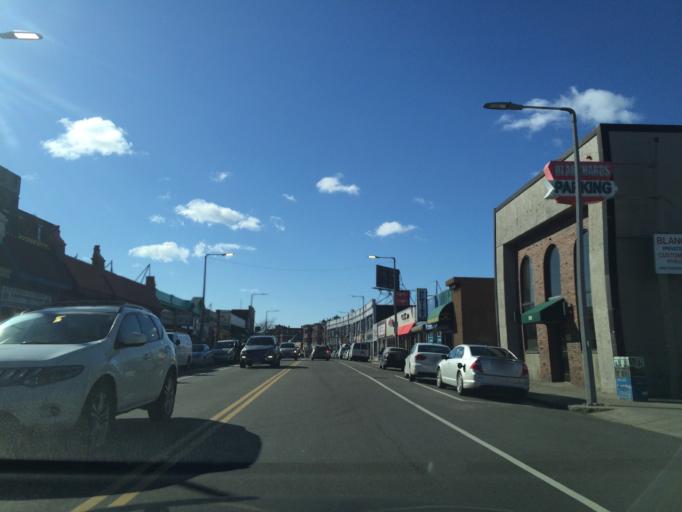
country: US
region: Massachusetts
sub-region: Norfolk County
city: Brookline
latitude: 42.3527
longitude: -71.1321
